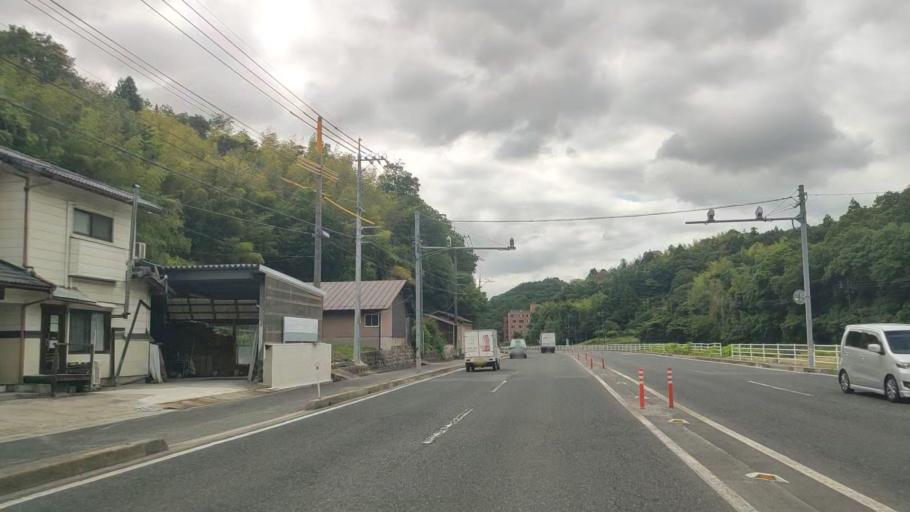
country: JP
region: Tottori
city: Yonago
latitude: 35.4138
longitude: 133.3540
